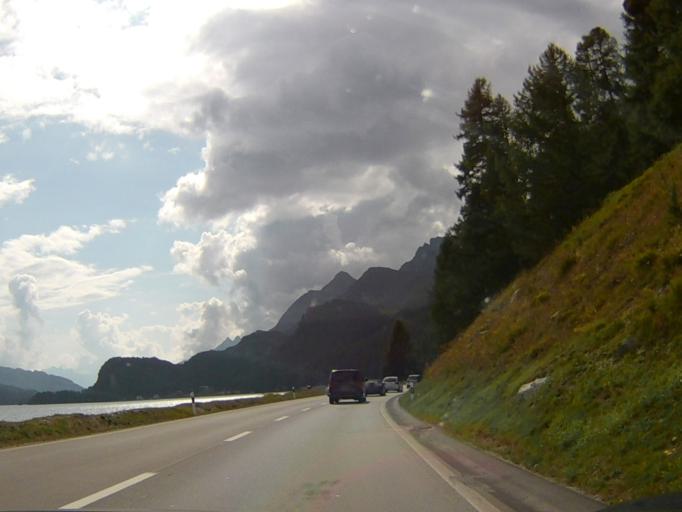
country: CH
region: Grisons
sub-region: Maloja District
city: Silvaplana
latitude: 46.4330
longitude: 9.7492
